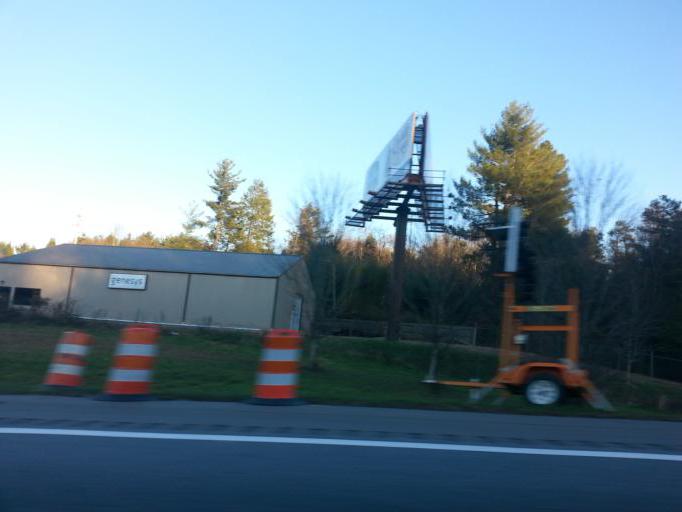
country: US
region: North Carolina
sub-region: Buncombe County
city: Bent Creek
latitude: 35.5428
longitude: -82.6037
